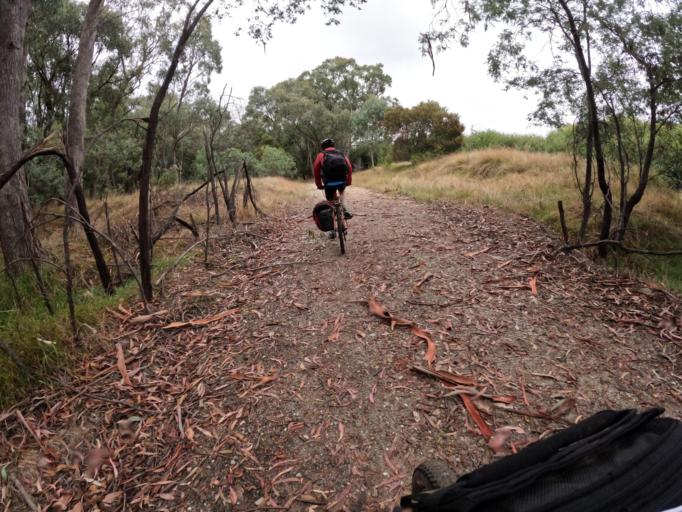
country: AU
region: New South Wales
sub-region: Greater Hume Shire
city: Holbrook
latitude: -36.1645
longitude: 147.4058
